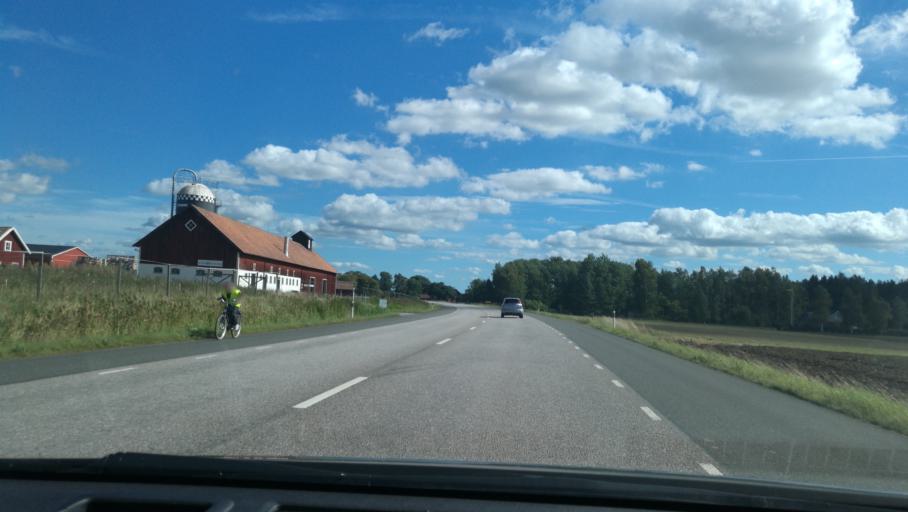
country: SE
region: Vaestra Goetaland
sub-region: Gotene Kommun
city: Kallby
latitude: 58.5087
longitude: 13.3837
